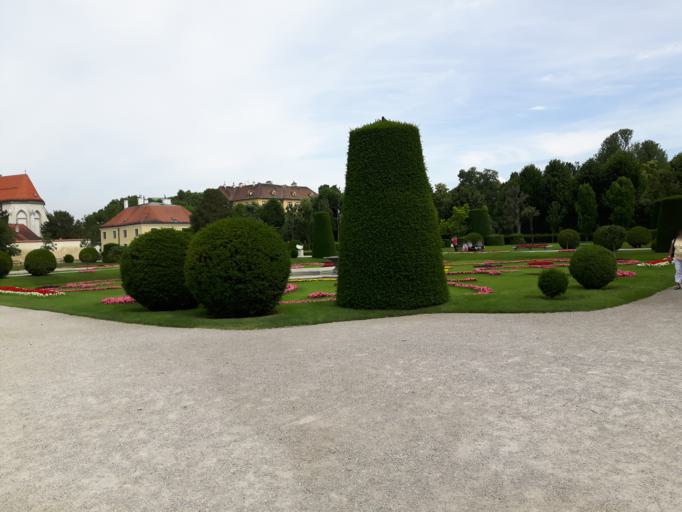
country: AT
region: Vienna
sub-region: Wien Stadt
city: Vienna
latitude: 48.1848
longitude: 16.3039
